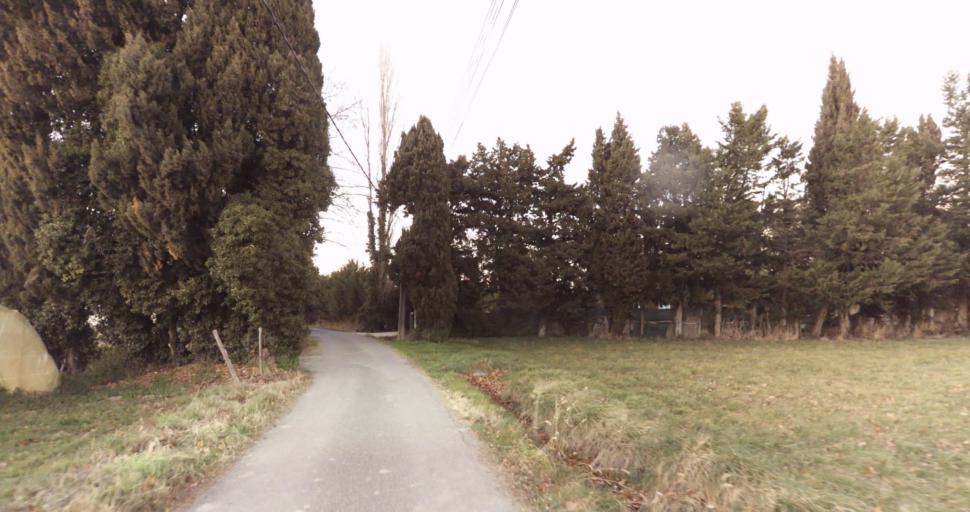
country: FR
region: Provence-Alpes-Cote d'Azur
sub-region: Departement des Bouches-du-Rhone
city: Rognonas
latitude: 43.9099
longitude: 4.7836
